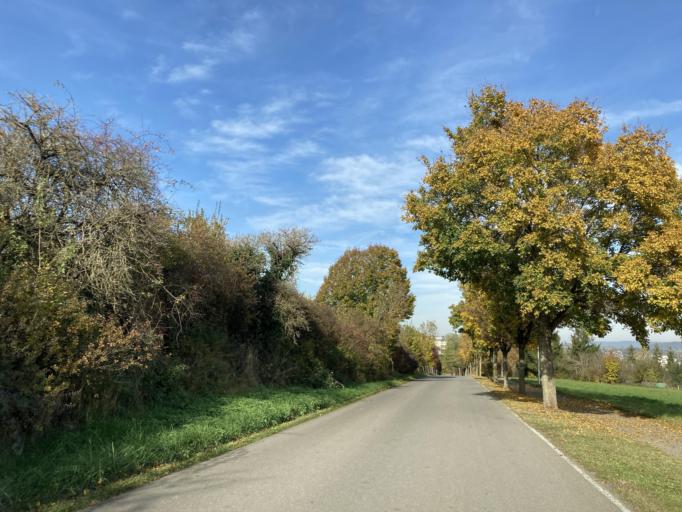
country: DE
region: Baden-Wuerttemberg
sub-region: Tuebingen Region
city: Rottenburg
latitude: 48.4594
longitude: 8.9396
